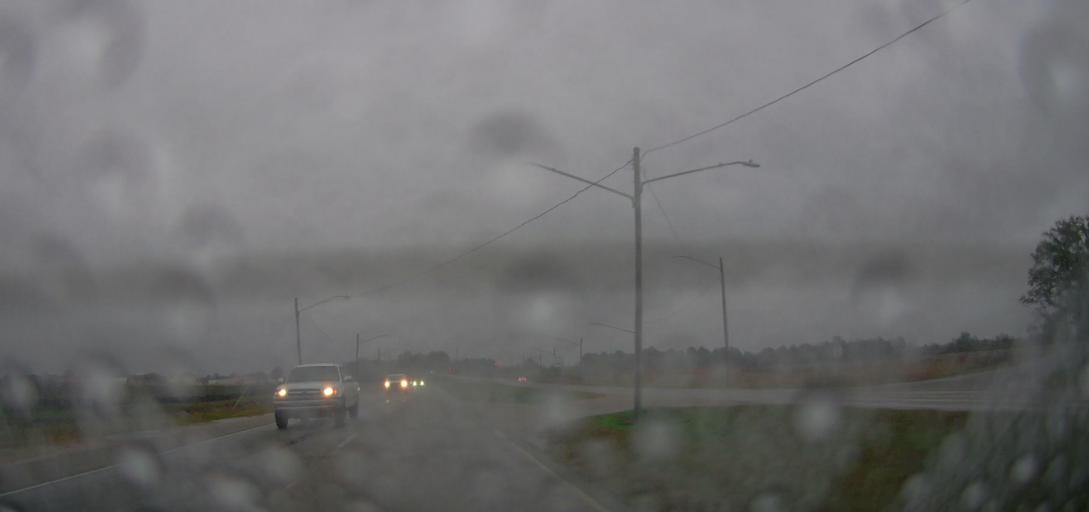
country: US
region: Alabama
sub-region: Montgomery County
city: Montgomery
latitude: 32.3678
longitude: -86.3585
